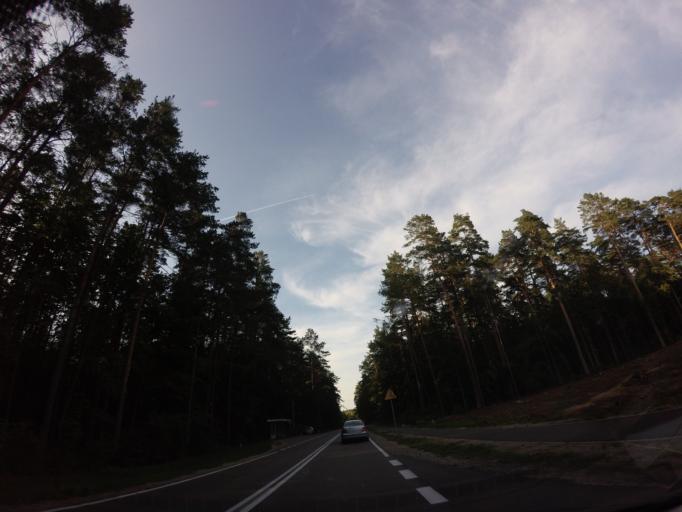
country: PL
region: Podlasie
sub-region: Powiat augustowski
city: Augustow
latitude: 53.8641
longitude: 23.0894
